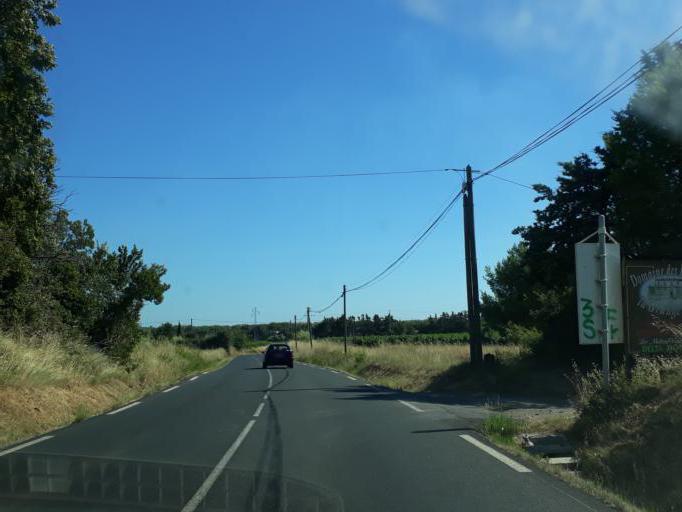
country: FR
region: Languedoc-Roussillon
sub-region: Departement de l'Herault
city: Agde
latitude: 43.3397
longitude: 3.4842
